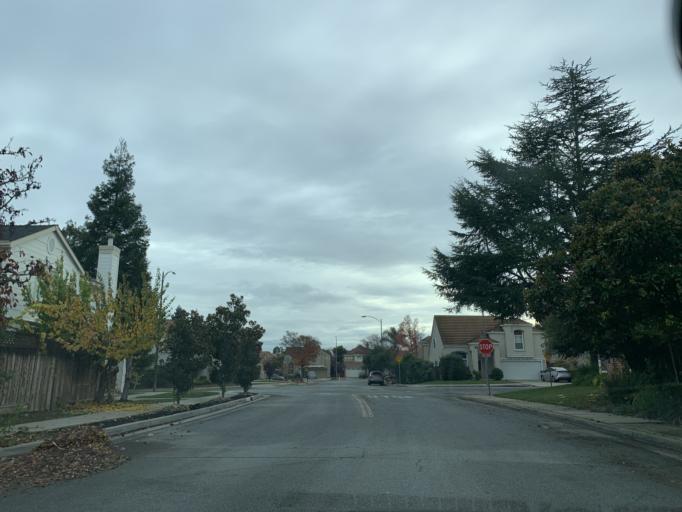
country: US
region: California
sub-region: Santa Clara County
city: Cambrian Park
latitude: 37.2539
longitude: -121.9409
